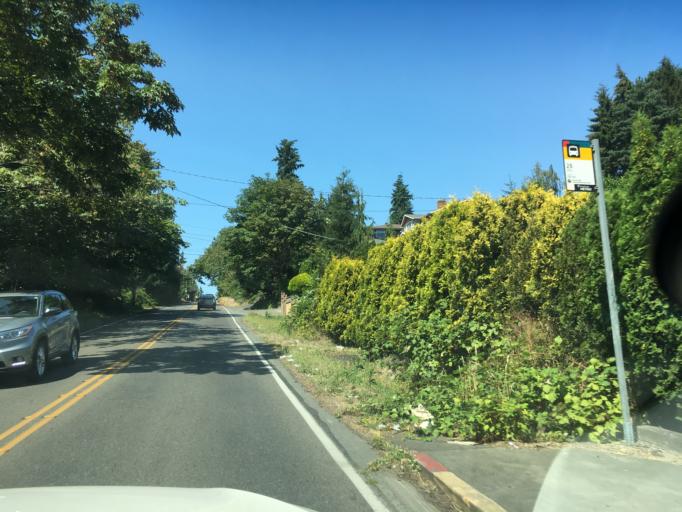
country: US
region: Washington
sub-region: King County
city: Shoreline
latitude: 47.7124
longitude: -122.3609
